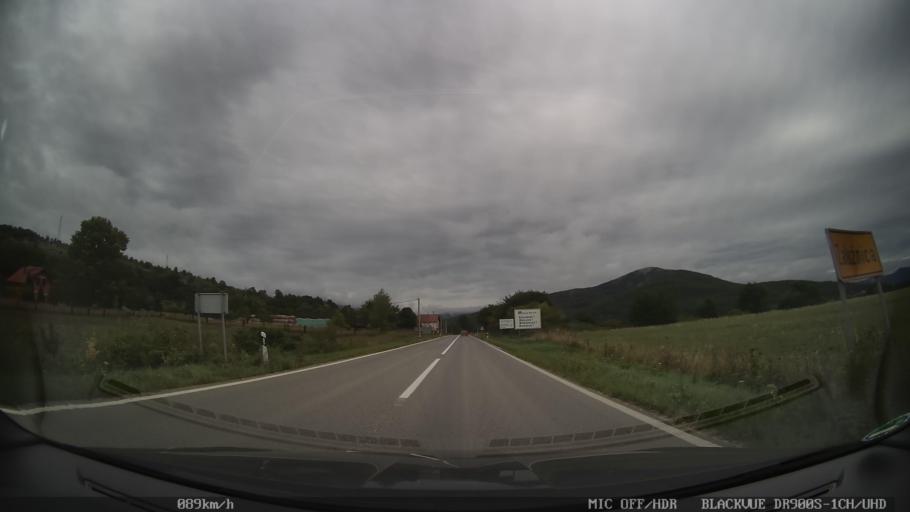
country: HR
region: Licko-Senjska
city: Otocac
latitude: 44.8575
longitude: 15.3230
